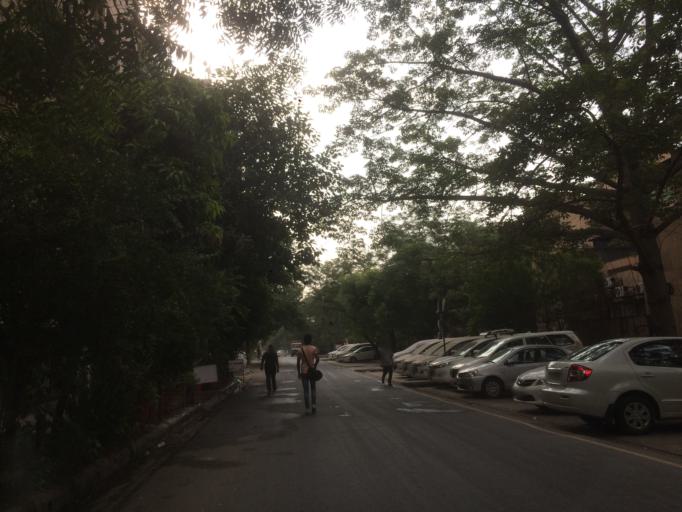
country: IN
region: NCT
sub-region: New Delhi
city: New Delhi
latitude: 28.5673
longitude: 77.1867
